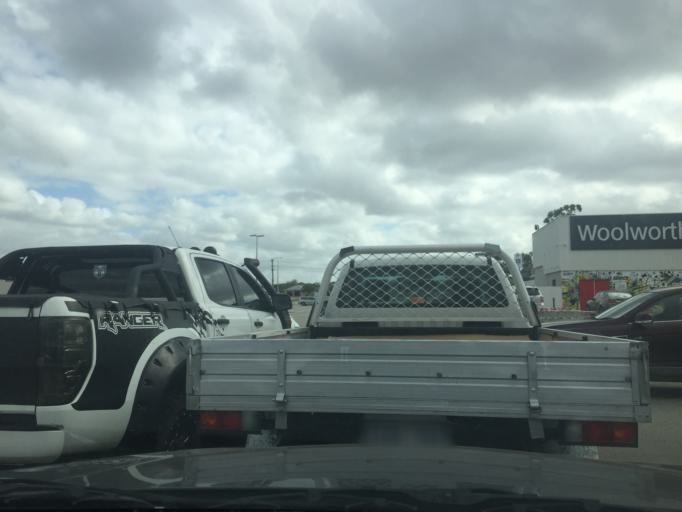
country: AU
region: Western Australia
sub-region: Gosnells
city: Maddington
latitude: -32.0535
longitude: 115.9796
